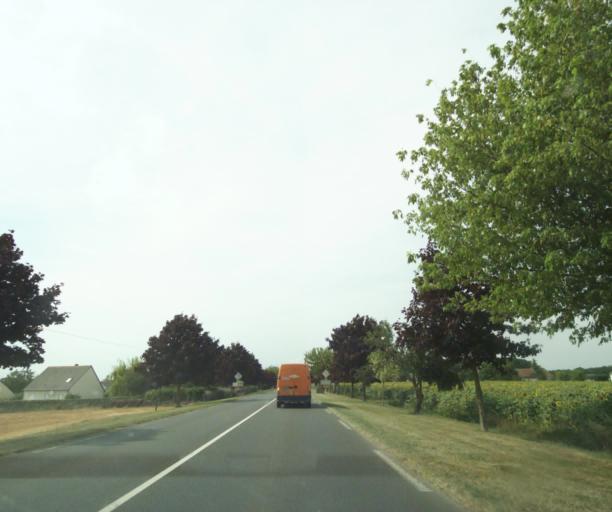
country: FR
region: Centre
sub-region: Departement d'Indre-et-Loire
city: Neuille-Pont-Pierre
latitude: 47.5422
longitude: 0.5548
